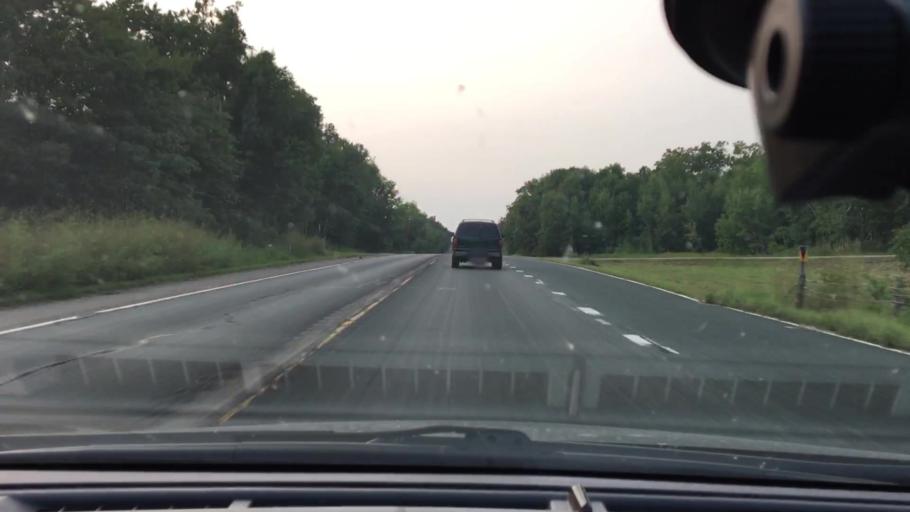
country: US
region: Minnesota
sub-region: Mille Lacs County
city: Vineland
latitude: 46.2418
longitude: -93.8062
